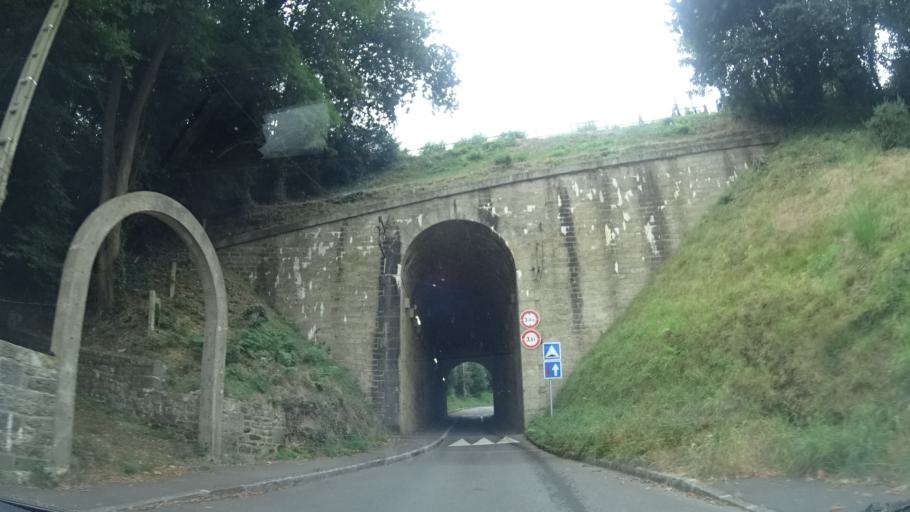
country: FR
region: Brittany
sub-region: Departement du Finistere
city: Brest
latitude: 48.3940
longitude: -4.4488
